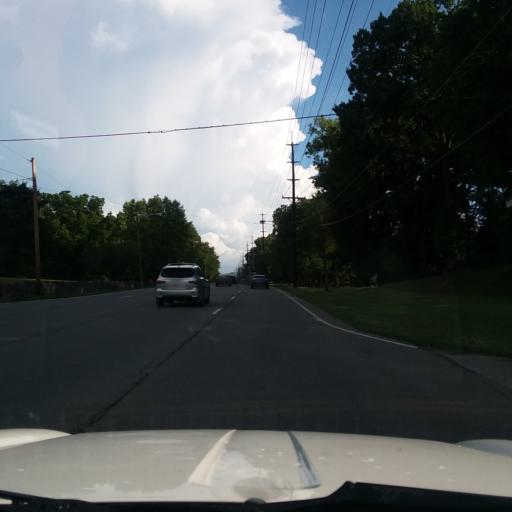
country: US
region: Tennessee
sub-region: Davidson County
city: Oak Hill
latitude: 36.0721
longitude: -86.7742
